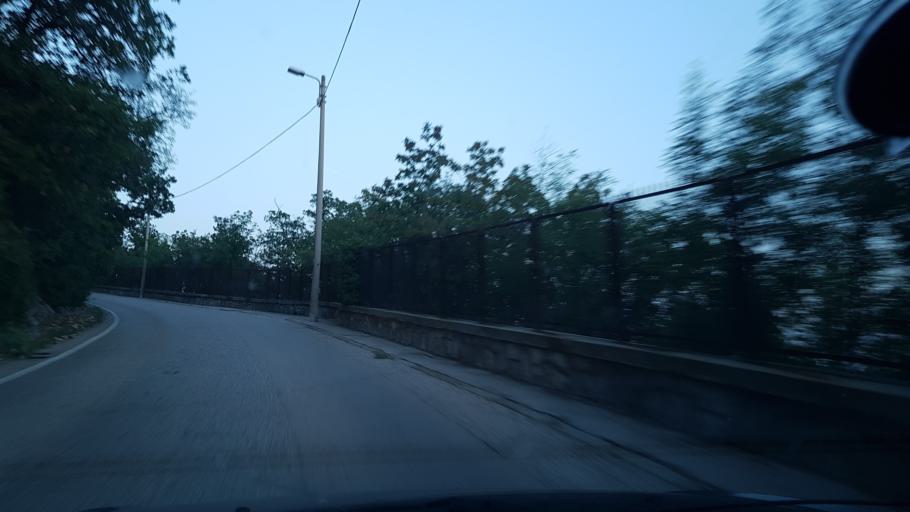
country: IT
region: Friuli Venezia Giulia
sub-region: Provincia di Trieste
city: Villa Opicina
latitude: 45.6796
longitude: 13.7769
